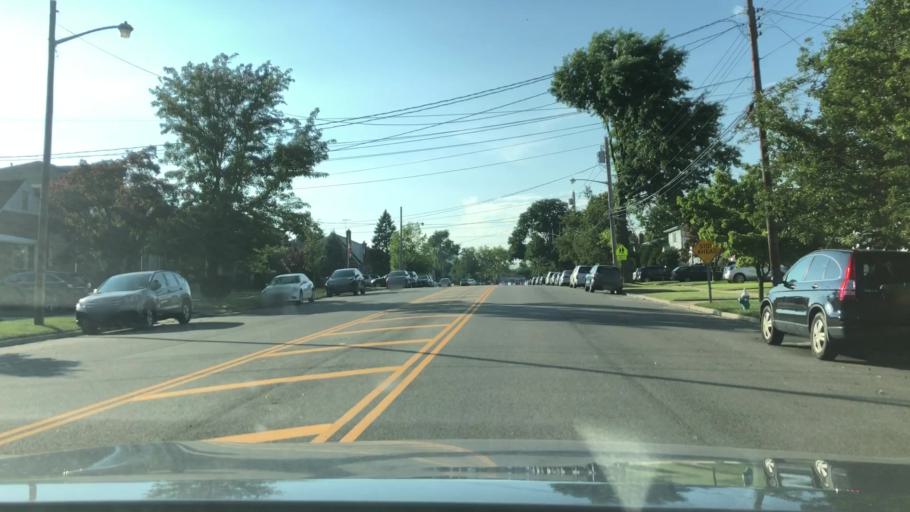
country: US
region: New York
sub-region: Nassau County
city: North New Hyde Park
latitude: 40.7375
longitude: -73.6949
